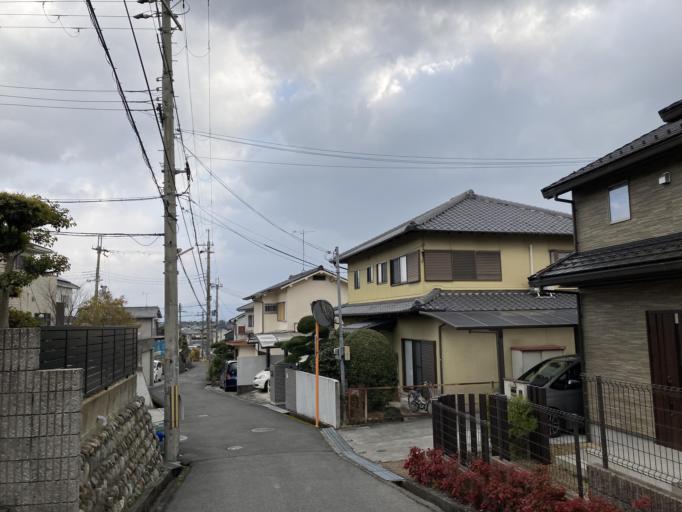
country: JP
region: Nara
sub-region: Ikoma-shi
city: Ikoma
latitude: 34.6105
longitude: 135.7261
